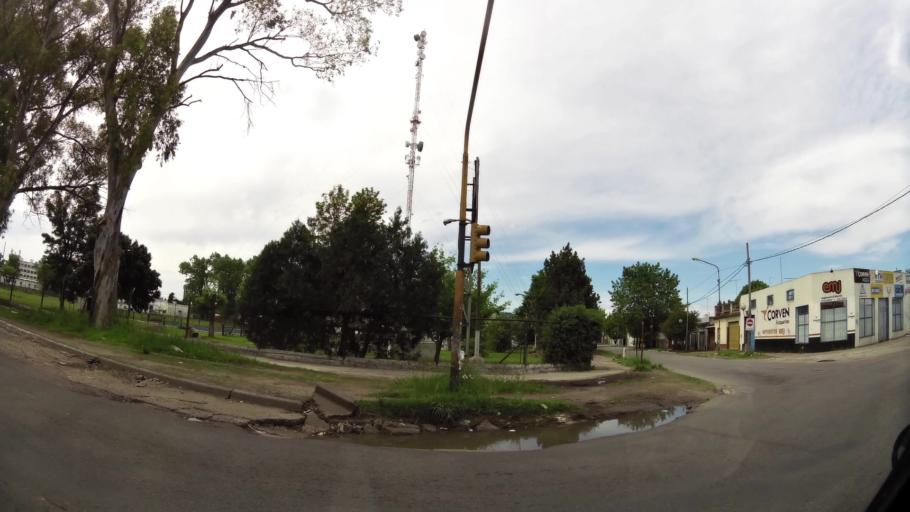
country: AR
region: Buenos Aires
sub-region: Partido de Quilmes
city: Quilmes
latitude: -34.7783
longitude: -58.2672
